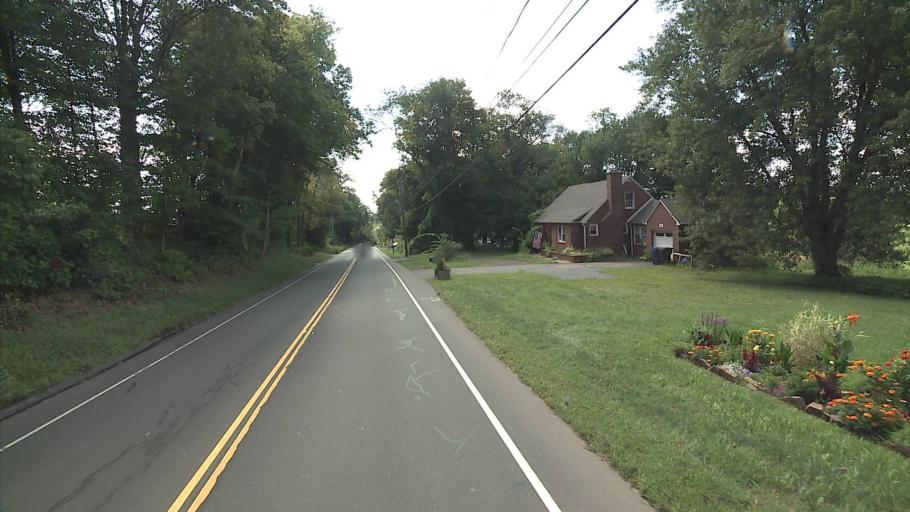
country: US
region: Connecticut
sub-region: Hartford County
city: Newington
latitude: 41.6459
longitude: -72.7158
